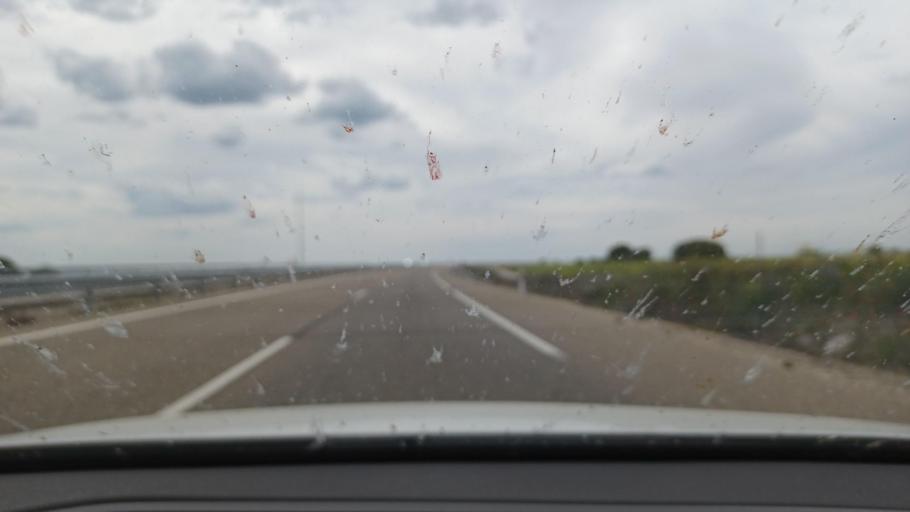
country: ES
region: Castille and Leon
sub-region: Provincia de Valladolid
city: San Miguel del Arroyo
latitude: 41.4353
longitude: -4.4299
